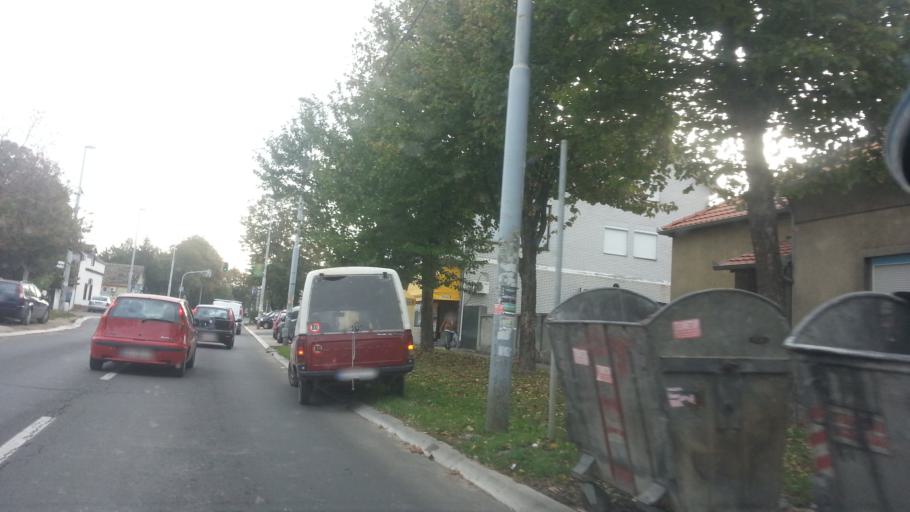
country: RS
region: Central Serbia
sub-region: Belgrade
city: Zemun
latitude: 44.8495
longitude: 20.3905
